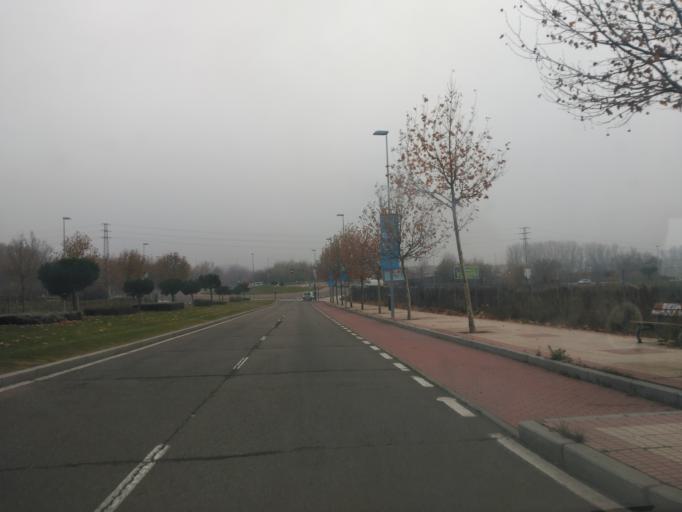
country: ES
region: Castille and Leon
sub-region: Provincia de Salamanca
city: Salamanca
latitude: 40.9627
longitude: -5.6456
